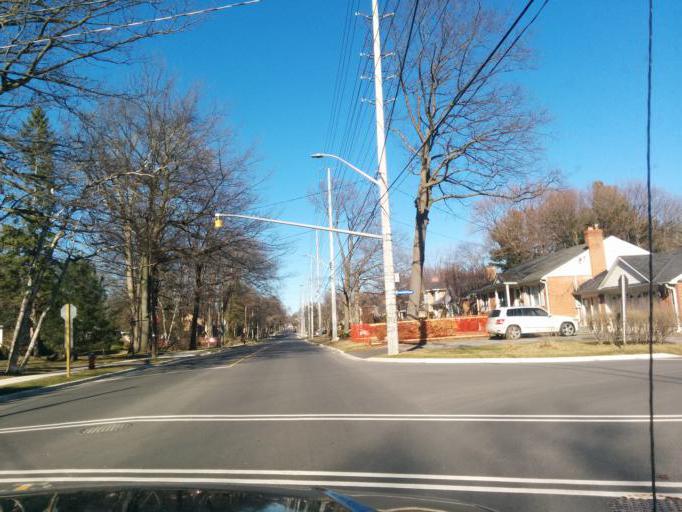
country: CA
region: Ontario
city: Mississauga
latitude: 43.5645
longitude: -79.5876
